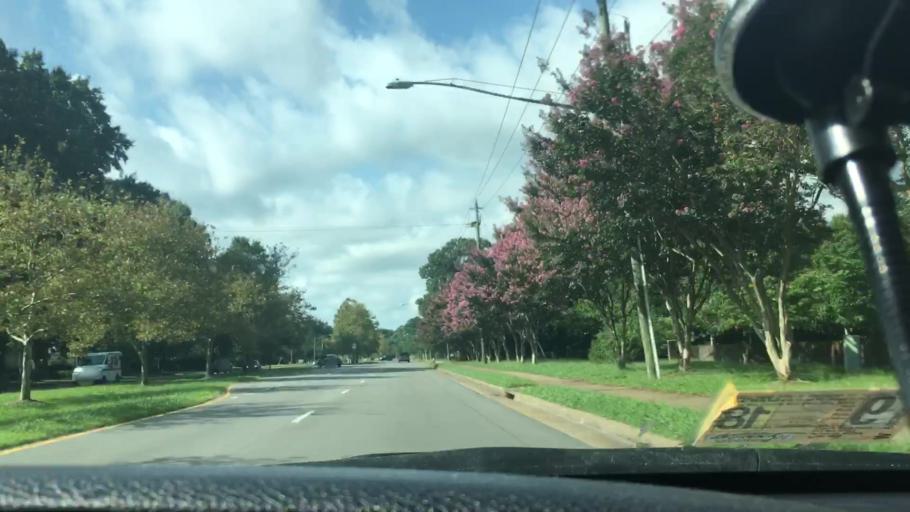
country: US
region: Virginia
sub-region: City of Virginia Beach
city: Virginia Beach
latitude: 36.8686
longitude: -76.0426
